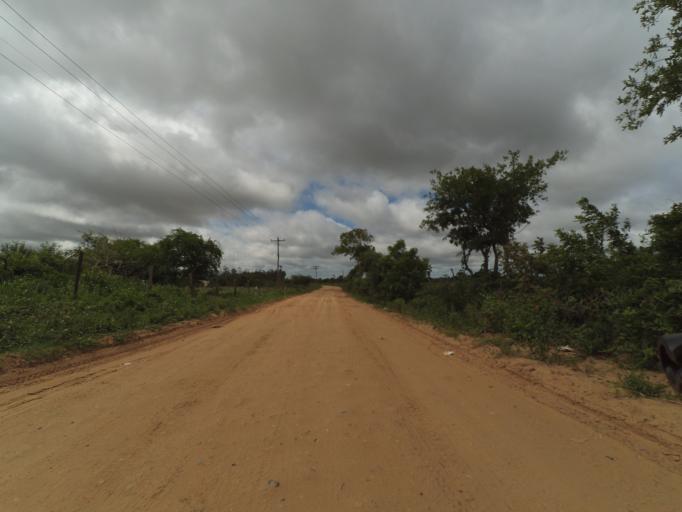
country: BO
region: Santa Cruz
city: Santa Cruz de la Sierra
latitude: -17.8926
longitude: -63.2409
